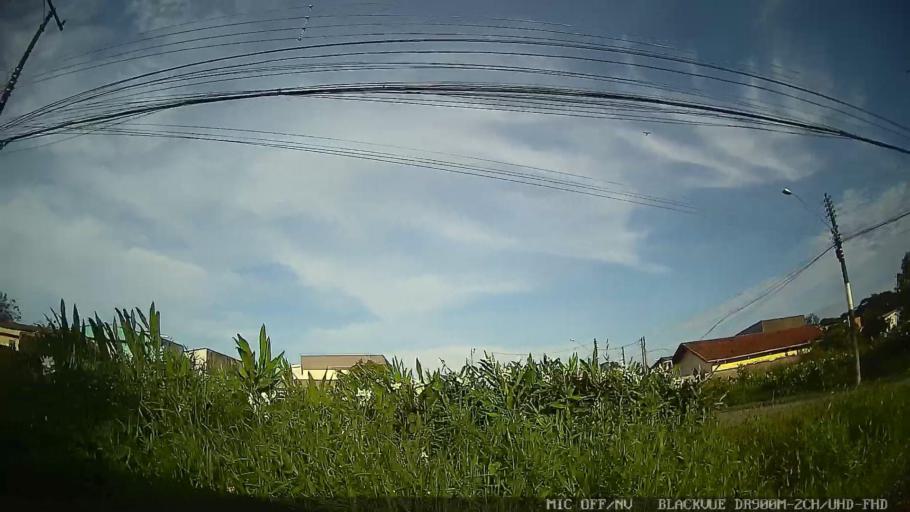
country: BR
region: Sao Paulo
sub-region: Itanhaem
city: Itanhaem
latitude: -24.1565
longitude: -46.7758
